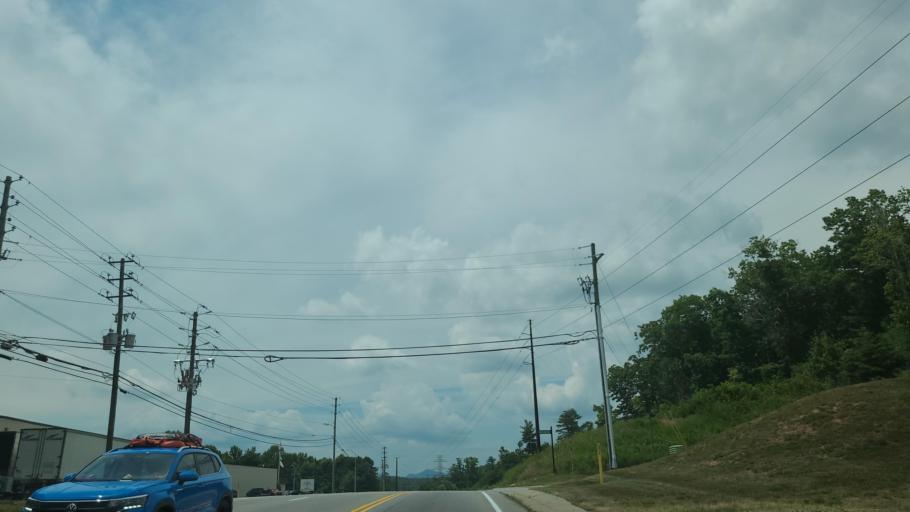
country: US
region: North Carolina
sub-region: Buncombe County
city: Avery Creek
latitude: 35.4806
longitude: -82.5660
